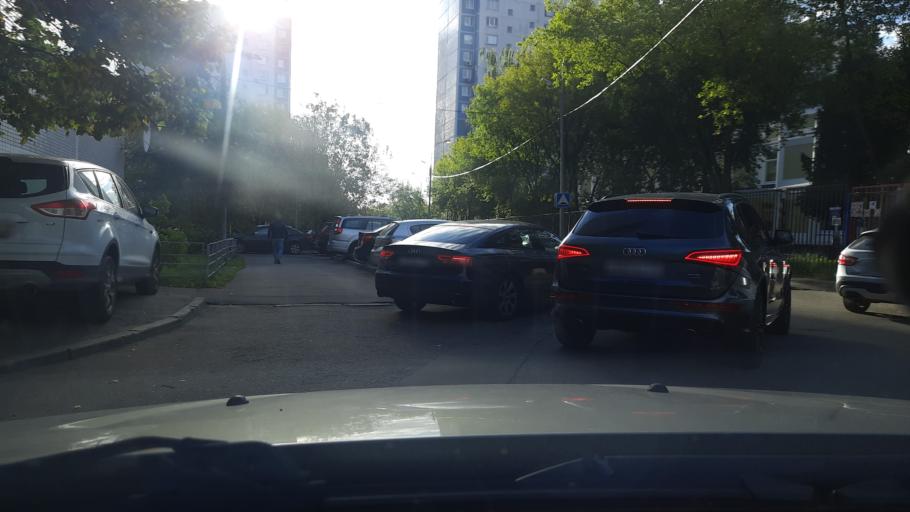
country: RU
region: Moscow
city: Strogino
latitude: 55.8072
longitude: 37.4203
